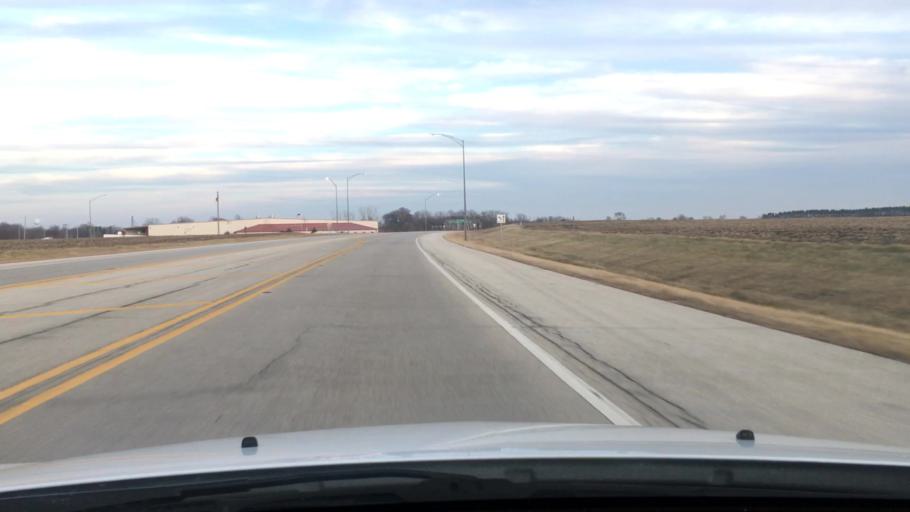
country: US
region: Illinois
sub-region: Livingston County
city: Chatsworth
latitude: 40.7508
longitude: -88.3140
